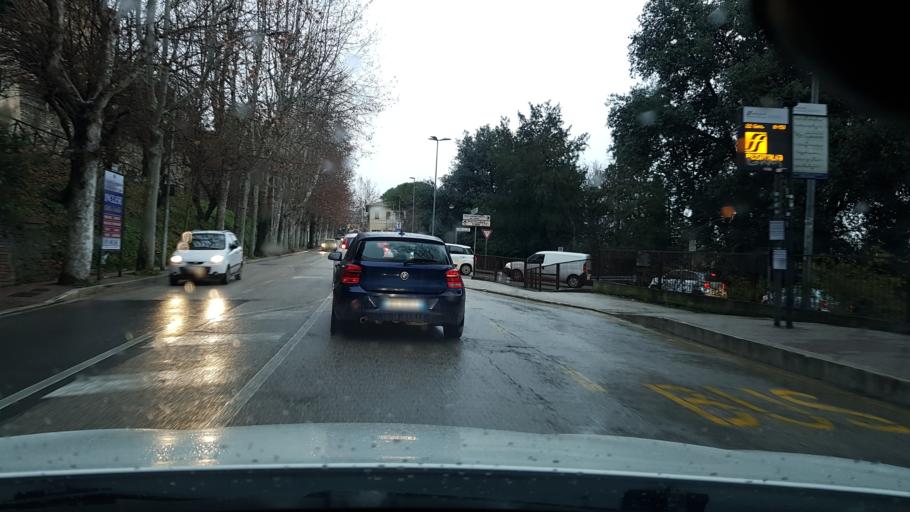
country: IT
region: Umbria
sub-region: Provincia di Perugia
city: Perugia
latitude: 43.1108
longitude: 12.3927
